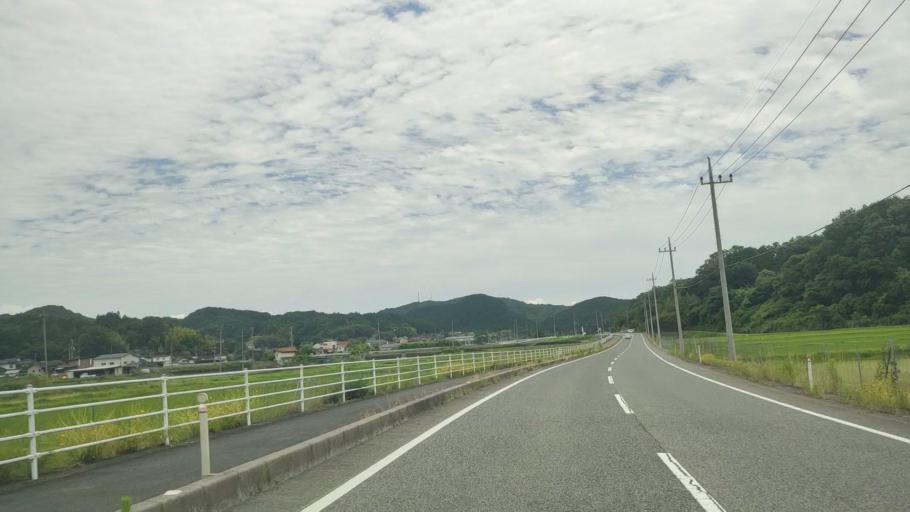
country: JP
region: Okayama
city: Tsuyama
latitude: 35.0656
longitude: 134.2004
